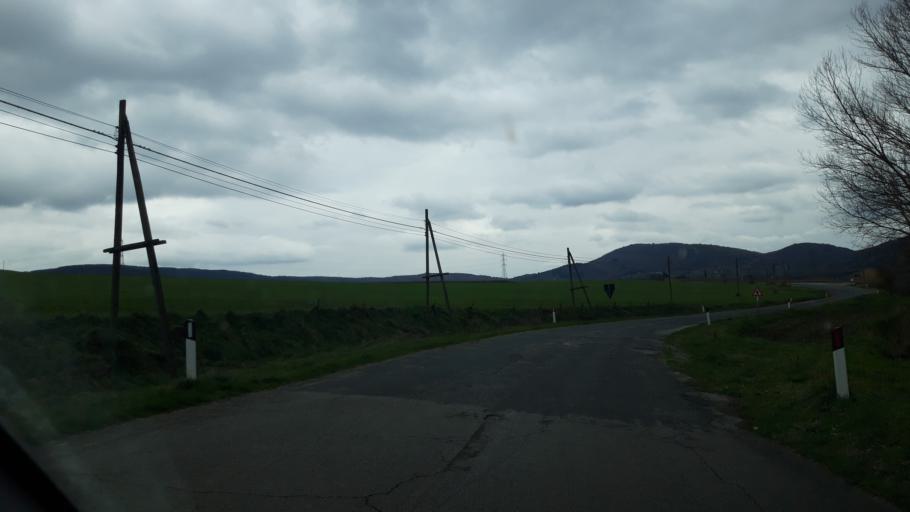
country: IT
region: Umbria
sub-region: Provincia di Perugia
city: Fontignano
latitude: 42.9959
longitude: 12.1889
